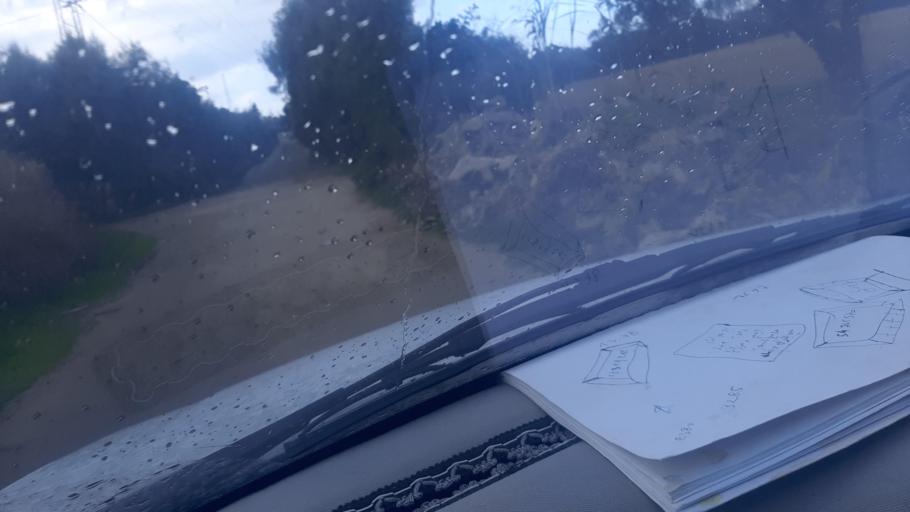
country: TN
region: Nabul
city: Manzil Bu Zalafah
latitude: 36.7408
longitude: 10.5291
